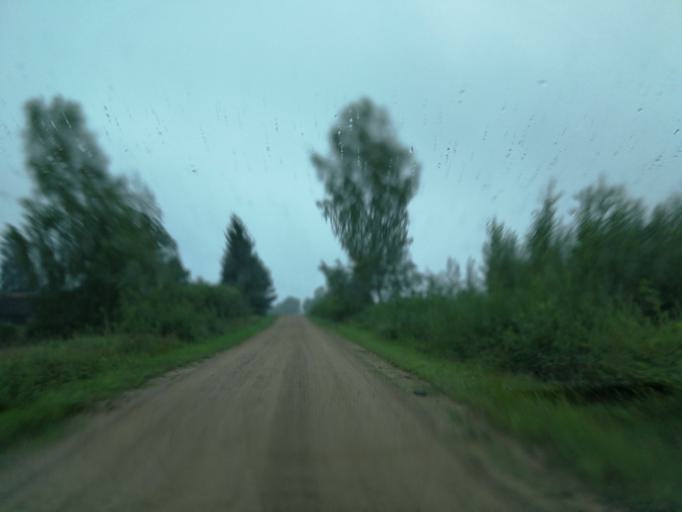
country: LV
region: Preilu Rajons
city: Jaunaglona
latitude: 56.3128
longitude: 27.0014
